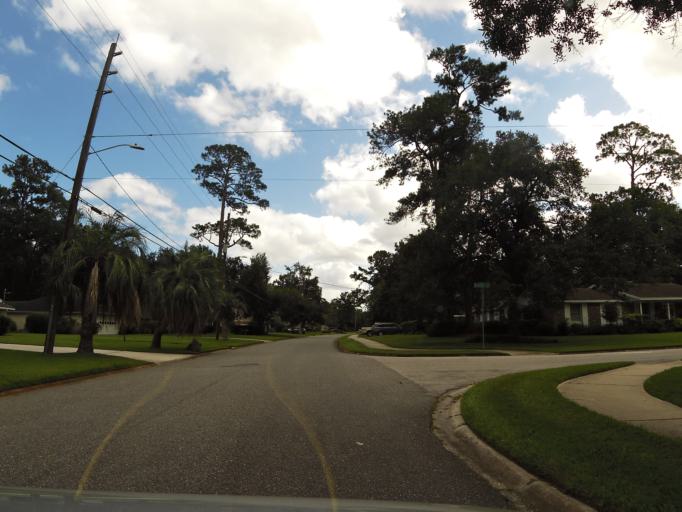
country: US
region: Florida
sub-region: Duval County
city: Jacksonville
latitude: 30.2586
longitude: -81.7019
